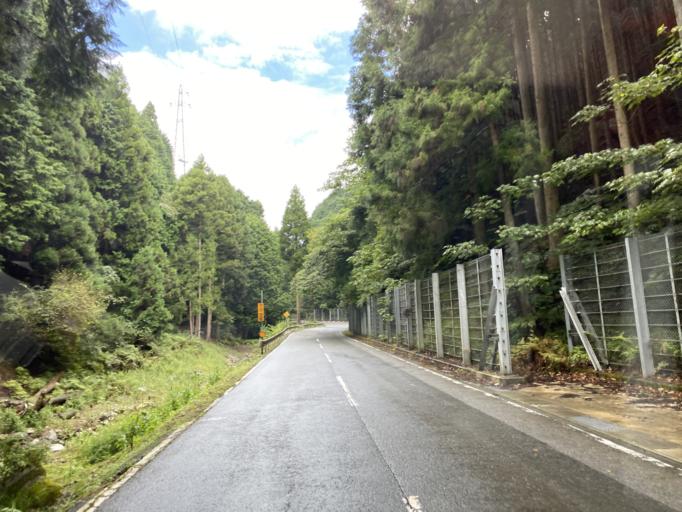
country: JP
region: Kyoto
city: Fukuchiyama
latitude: 35.3000
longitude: 134.9522
